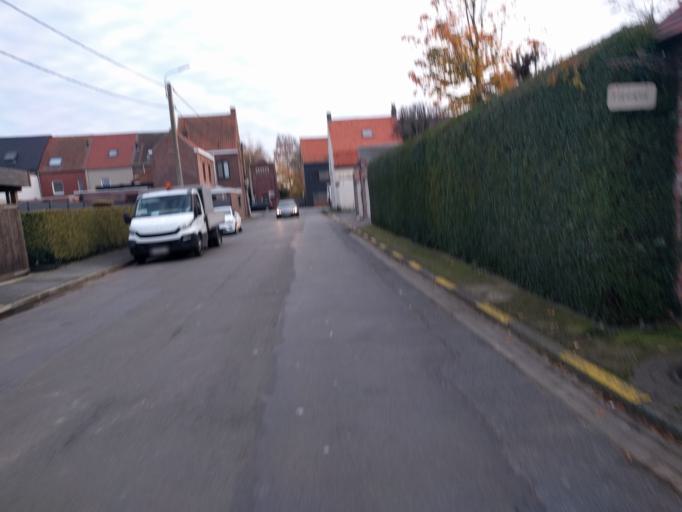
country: BE
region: Flanders
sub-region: Provincie West-Vlaanderen
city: Wevelgem
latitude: 50.8051
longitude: 3.1665
